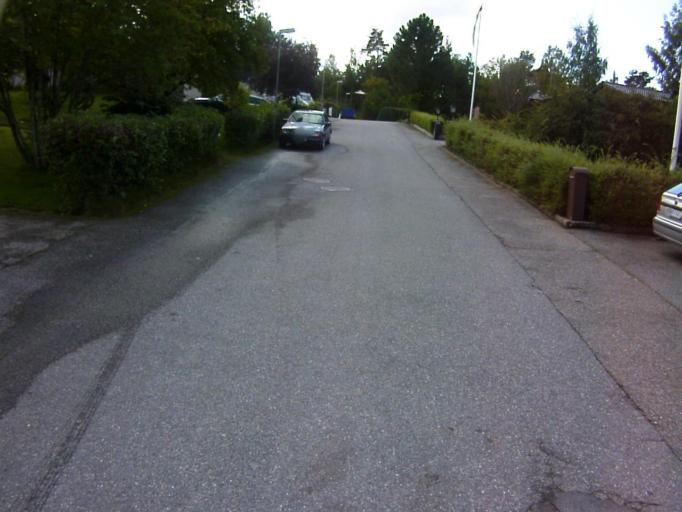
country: SE
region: Soedermanland
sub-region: Eskilstuna Kommun
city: Eskilstuna
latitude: 59.3980
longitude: 16.5394
